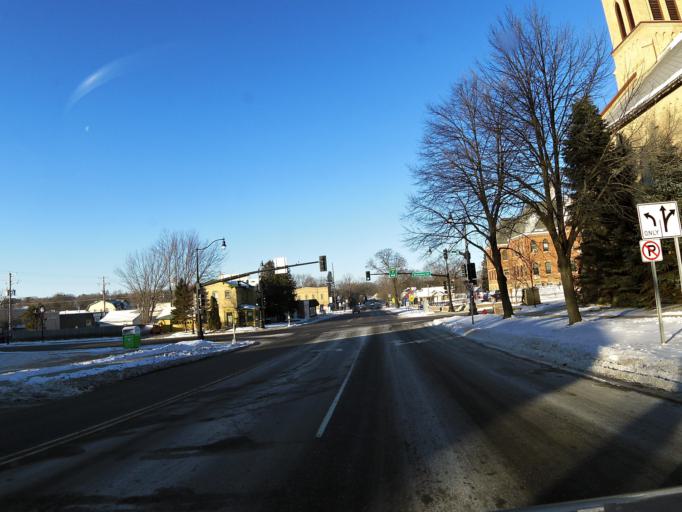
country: US
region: Minnesota
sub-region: Scott County
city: Jordan
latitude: 44.6674
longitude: -93.6253
